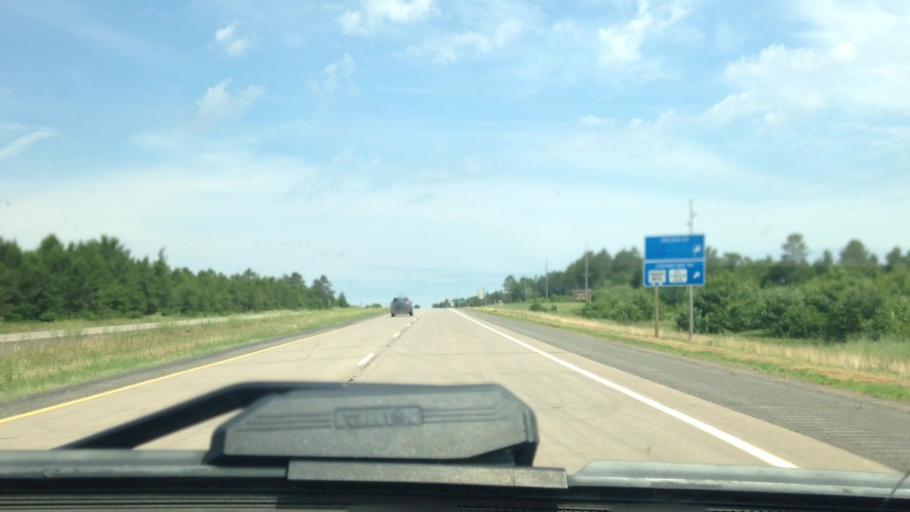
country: US
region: Wisconsin
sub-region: Douglas County
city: Lake Nebagamon
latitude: 46.3121
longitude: -91.8118
